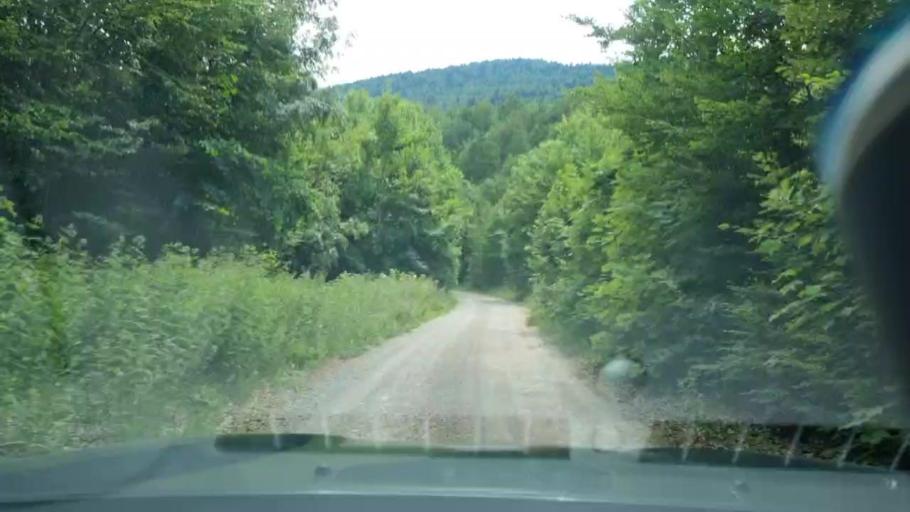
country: BA
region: Federation of Bosnia and Herzegovina
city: Bosansko Grahovo
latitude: 44.3172
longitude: 16.2454
